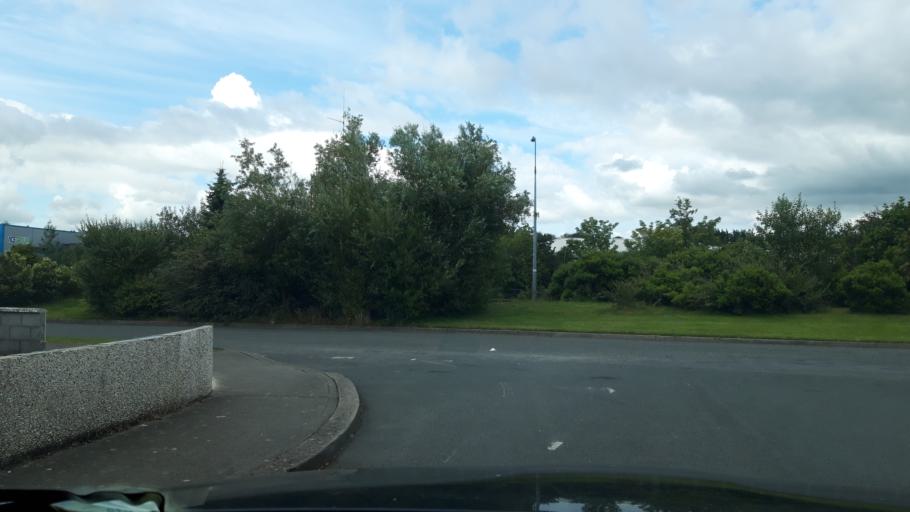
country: IE
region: Leinster
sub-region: Wicklow
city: Blessington
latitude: 53.1756
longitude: -6.5310
